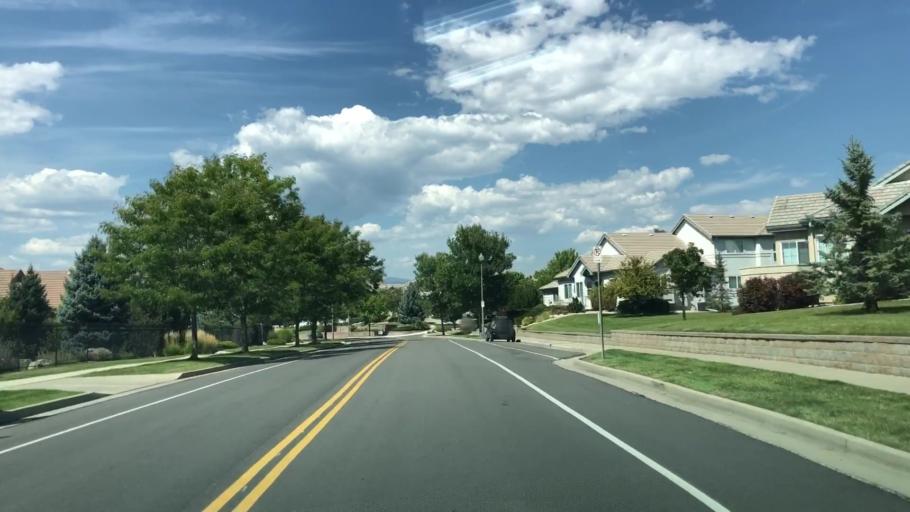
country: US
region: Colorado
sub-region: Larimer County
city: Loveland
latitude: 40.3965
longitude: -105.1441
